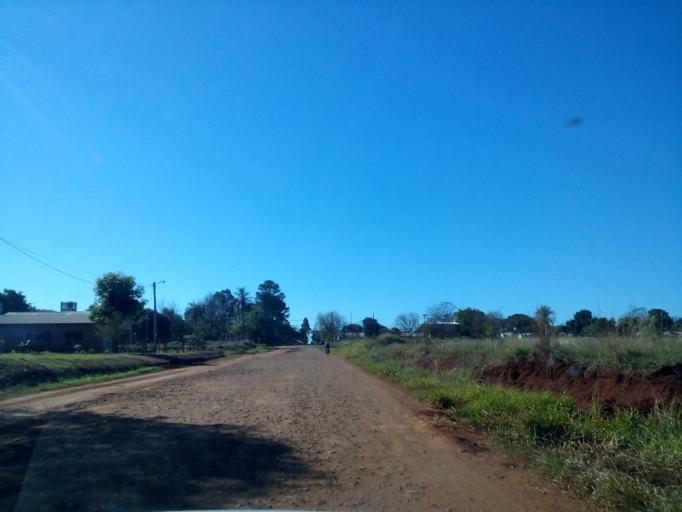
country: AR
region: Misiones
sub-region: Departamento de Capital
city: Posadas
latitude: -27.3795
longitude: -55.9428
